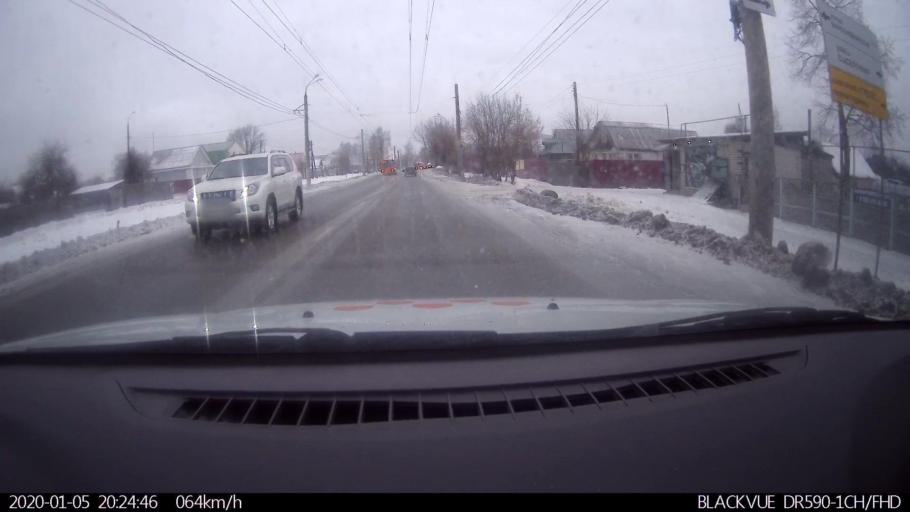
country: RU
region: Nizjnij Novgorod
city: Gorbatovka
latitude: 56.3850
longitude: 43.7813
